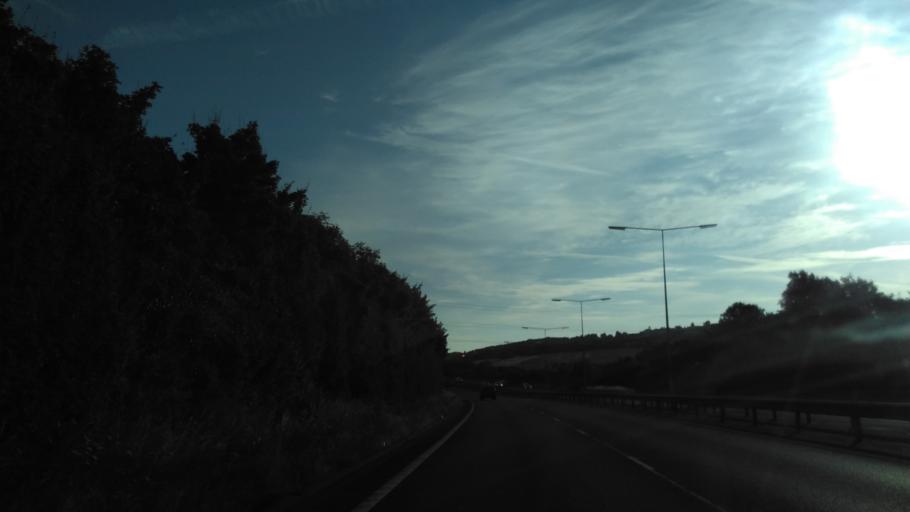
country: GB
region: England
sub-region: Kent
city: Whitstable
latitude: 51.3308
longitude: 0.9972
